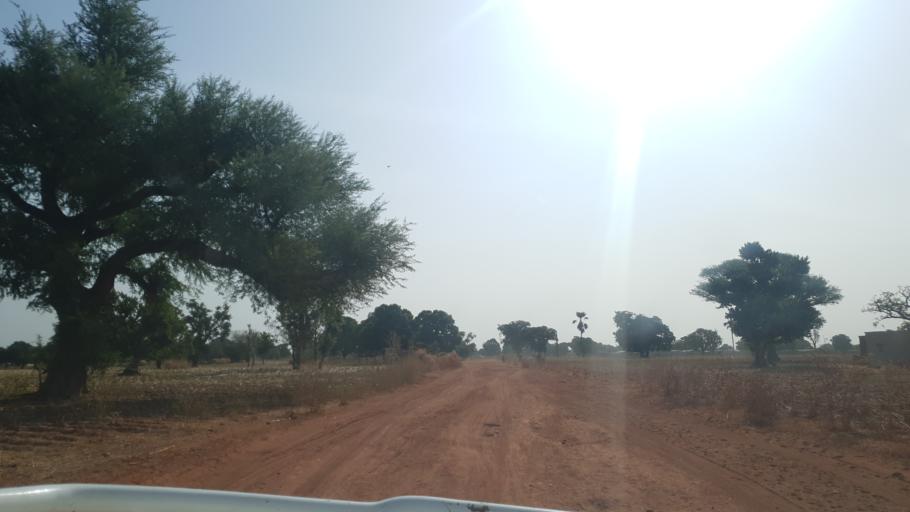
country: ML
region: Koulikoro
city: Dioila
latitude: 12.7071
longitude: -6.7736
